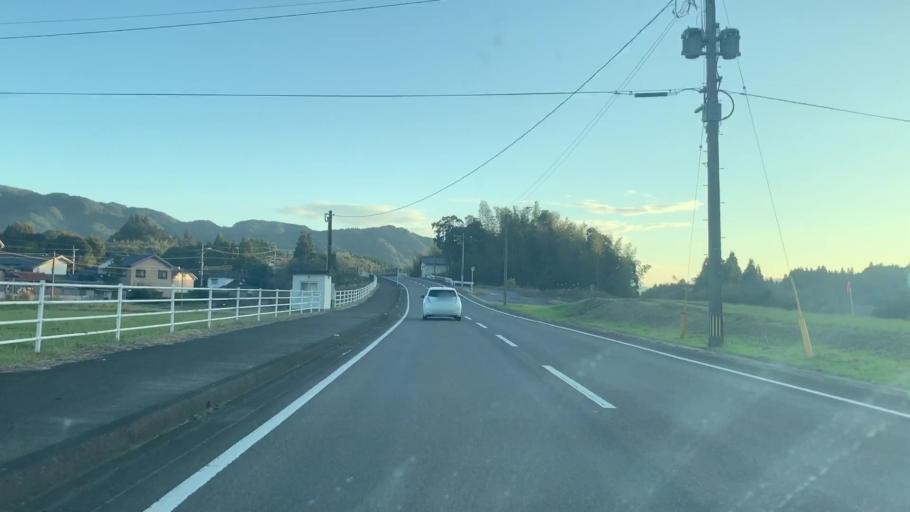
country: JP
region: Saga Prefecture
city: Imaricho-ko
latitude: 33.2939
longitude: 129.9699
